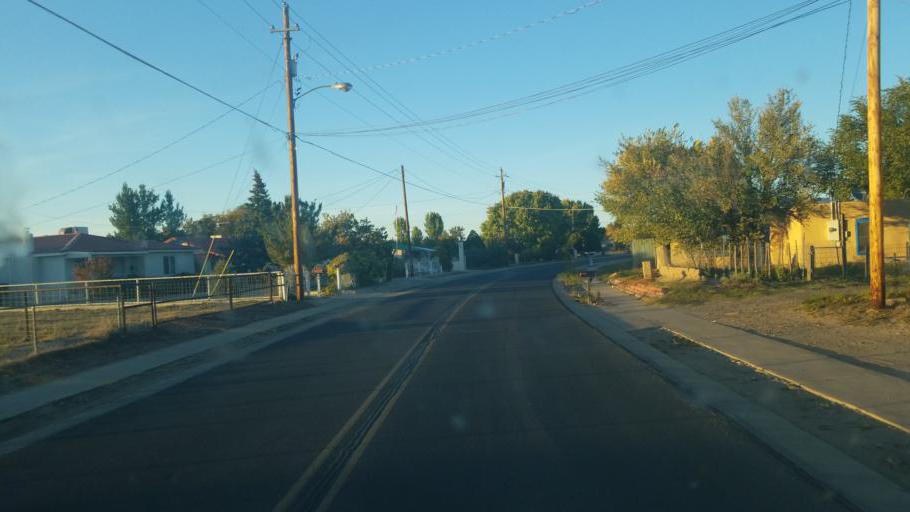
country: US
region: New Mexico
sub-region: Valencia County
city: Los Lunas
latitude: 34.8189
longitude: -106.7262
